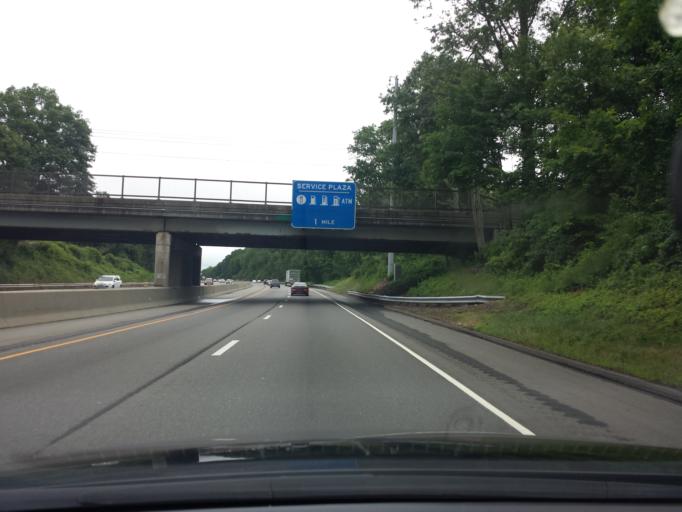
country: US
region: Connecticut
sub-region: New Haven County
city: Madison Center
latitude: 41.2876
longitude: -72.6027
